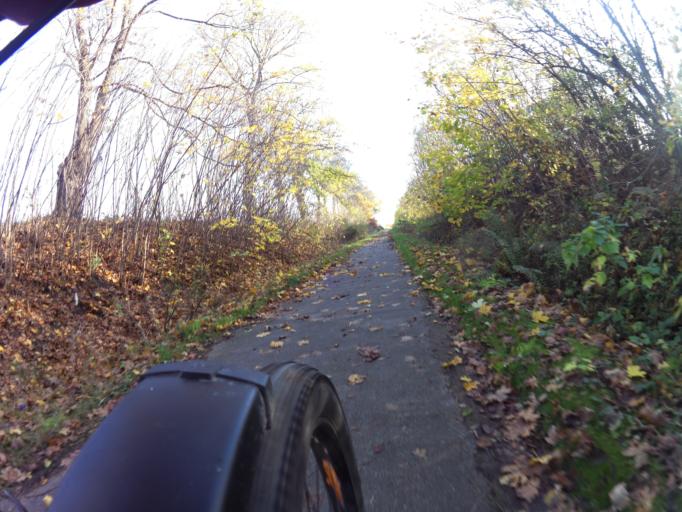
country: PL
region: Pomeranian Voivodeship
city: Strzelno
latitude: 54.7658
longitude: 18.2472
